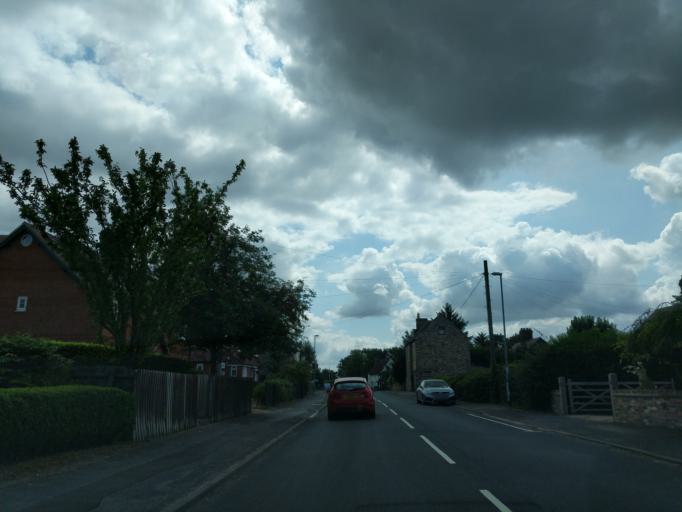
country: GB
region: England
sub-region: Cambridgeshire
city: Isleham
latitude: 52.3029
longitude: 0.4353
